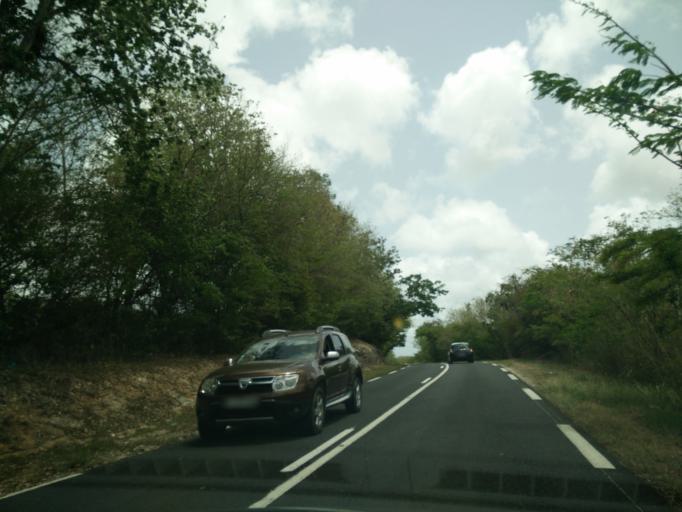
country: GP
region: Guadeloupe
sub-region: Guadeloupe
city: Petit-Canal
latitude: 16.4023
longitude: -61.5039
